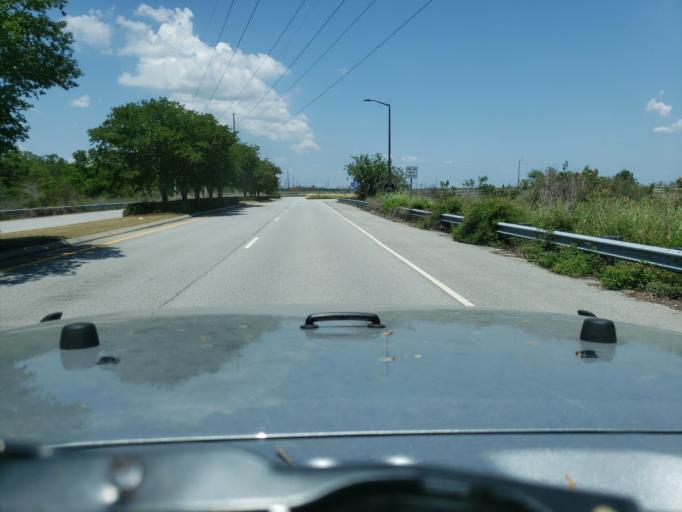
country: US
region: Georgia
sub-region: Chatham County
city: Savannah
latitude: 32.0965
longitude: -81.0945
